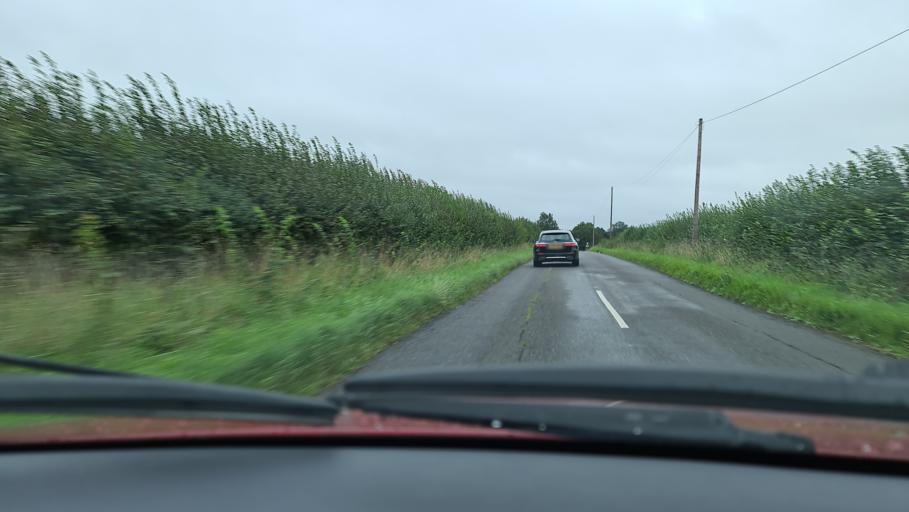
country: GB
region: England
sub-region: Oxfordshire
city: Bicester
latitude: 51.9292
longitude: -1.1900
